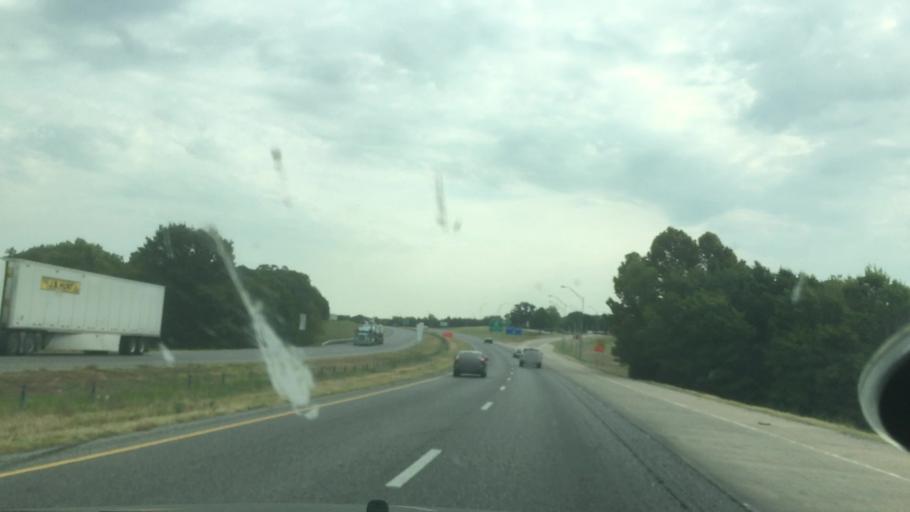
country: US
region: Oklahoma
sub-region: Bryan County
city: Colbert
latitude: 33.8408
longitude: -96.5167
